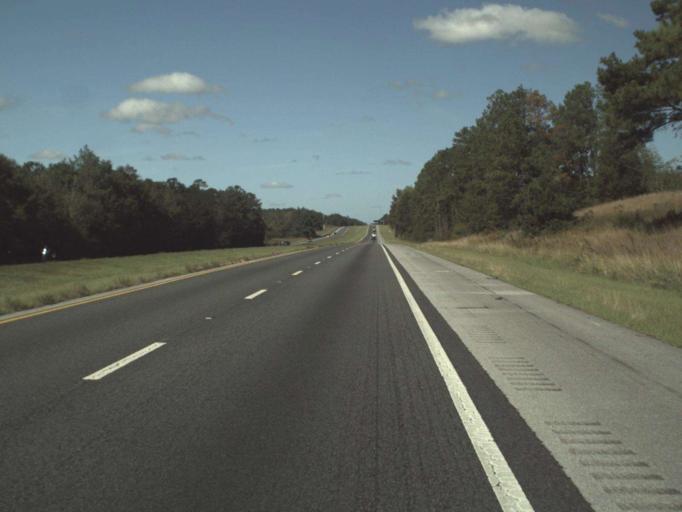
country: US
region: Florida
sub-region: Jackson County
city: Marianna
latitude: 30.6882
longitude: -85.1133
